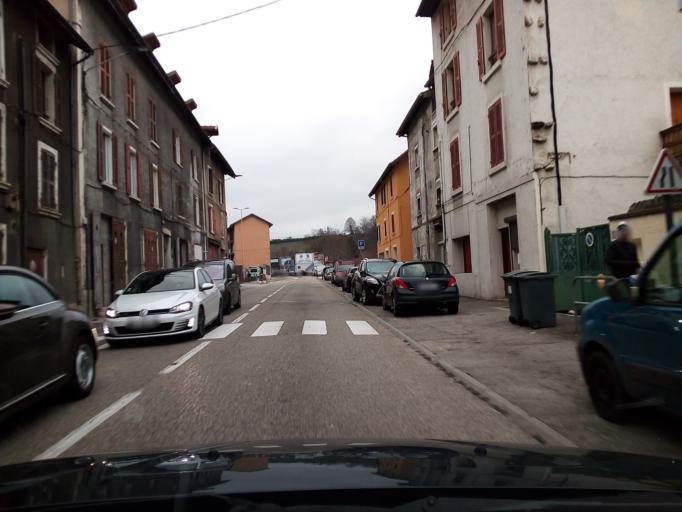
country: FR
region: Rhone-Alpes
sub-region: Departement de l'Isere
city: Saint-Jean-de-Moirans
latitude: 45.3522
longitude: 5.5913
